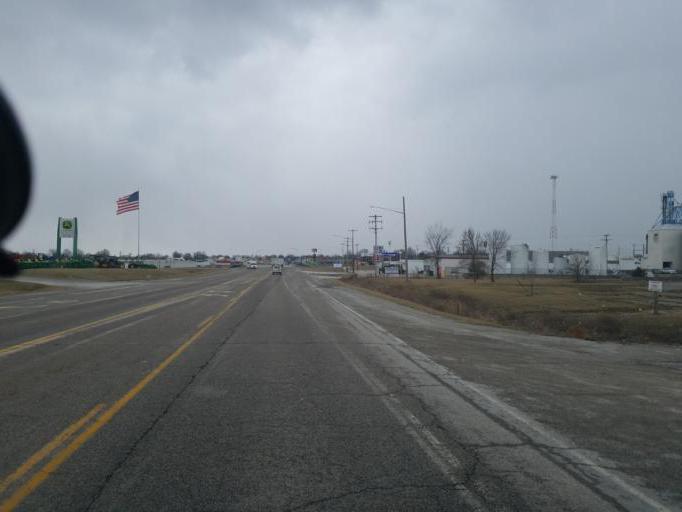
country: US
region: Missouri
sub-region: Macon County
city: Macon
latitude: 39.7570
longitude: -92.4678
